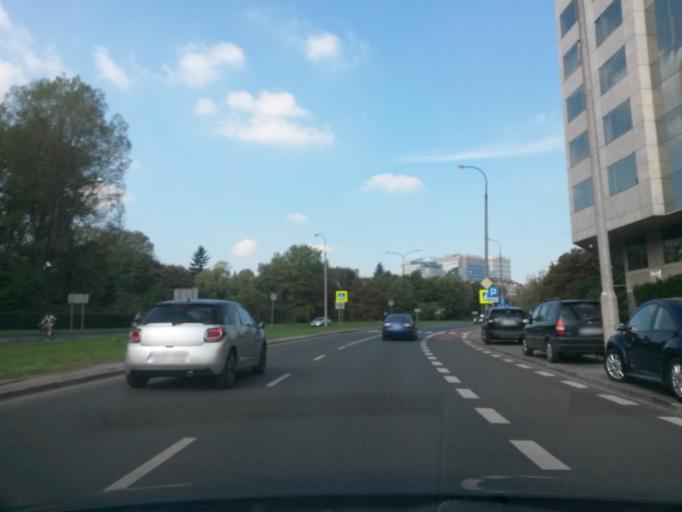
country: PL
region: Masovian Voivodeship
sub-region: Warszawa
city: Mokotow
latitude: 52.2072
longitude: 21.0291
